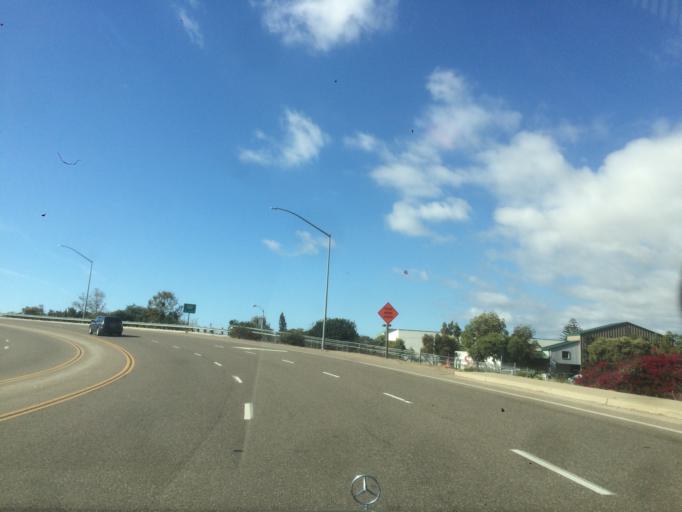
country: US
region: California
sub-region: Santa Barbara County
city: Goleta
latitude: 34.4408
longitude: -119.8314
